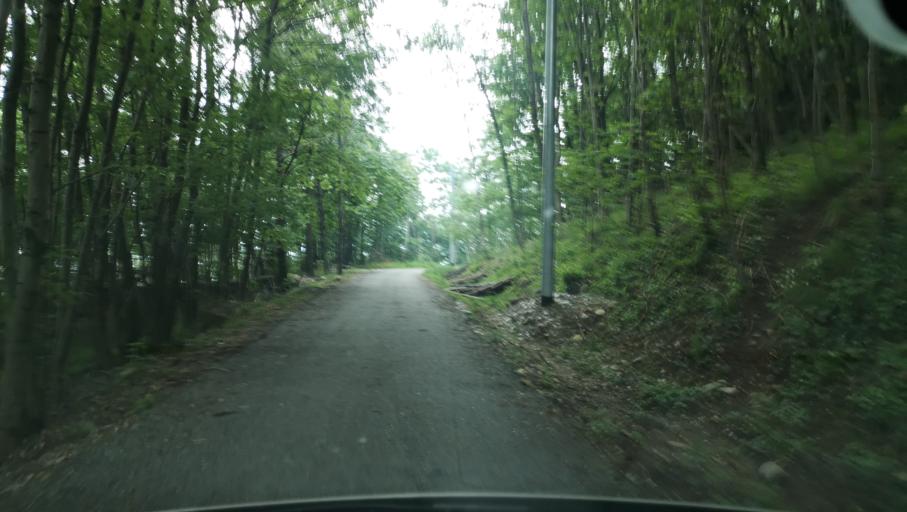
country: IT
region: Piedmont
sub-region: Provincia di Torino
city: Tavagnasco
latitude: 45.5319
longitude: 7.8195
